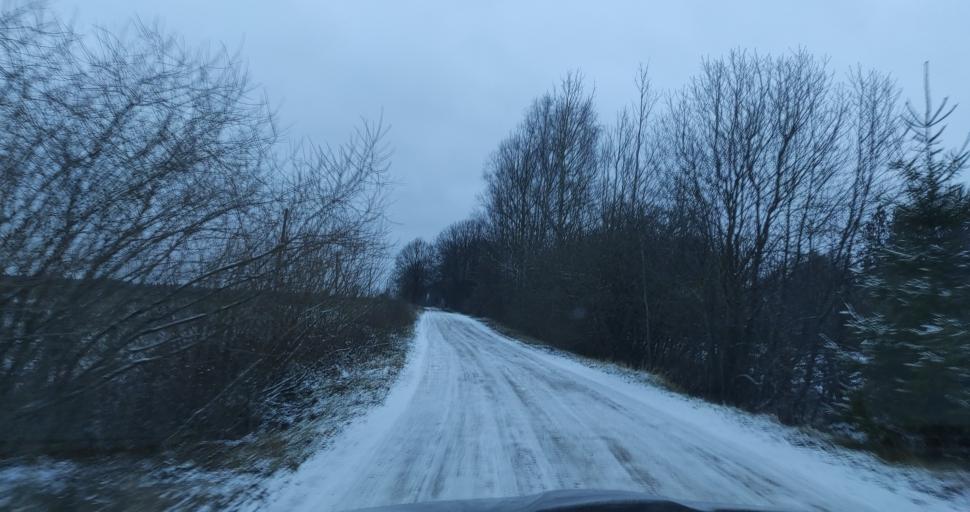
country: LV
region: Kuldigas Rajons
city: Kuldiga
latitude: 56.9687
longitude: 22.0635
